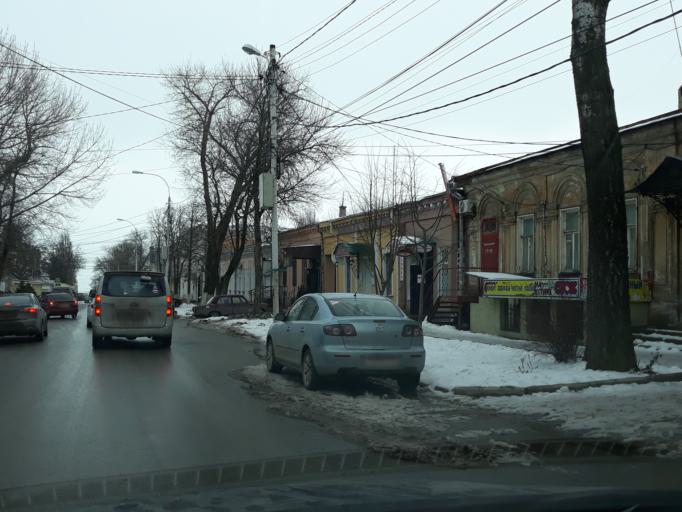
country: RU
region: Rostov
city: Taganrog
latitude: 47.2112
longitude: 38.9332
